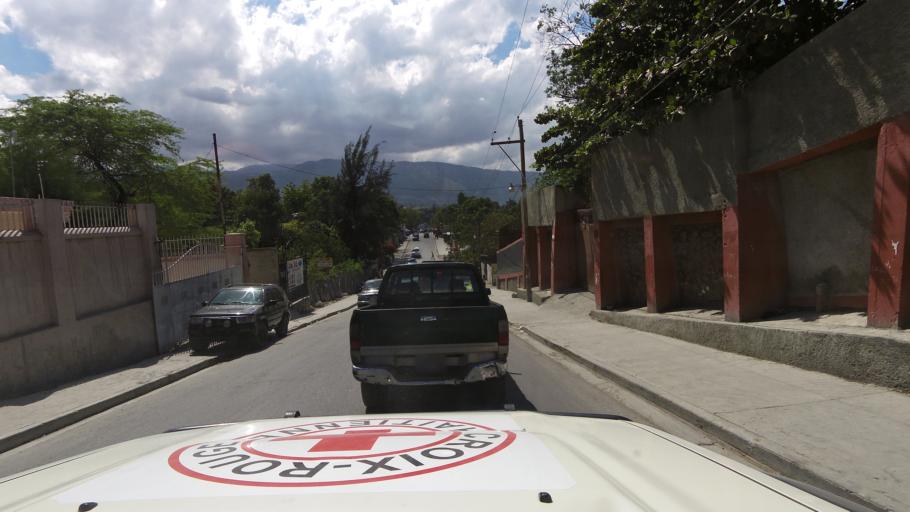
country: HT
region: Ouest
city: Delmas 73
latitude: 18.5627
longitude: -72.3004
